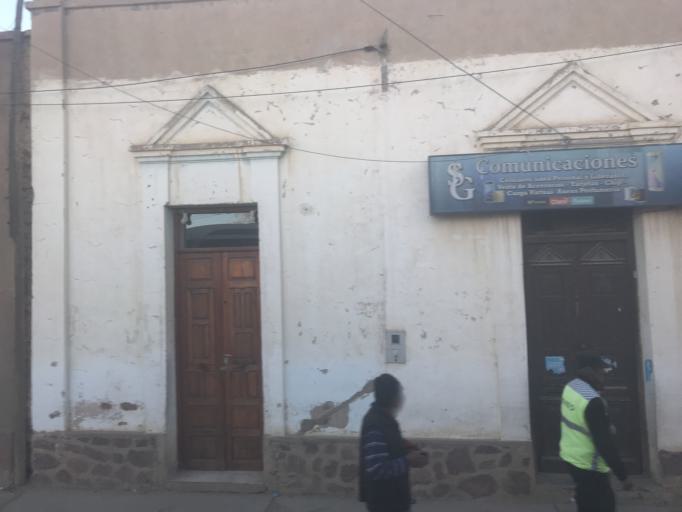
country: AR
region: Jujuy
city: Abra Pampa
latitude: -22.7213
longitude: -65.6974
